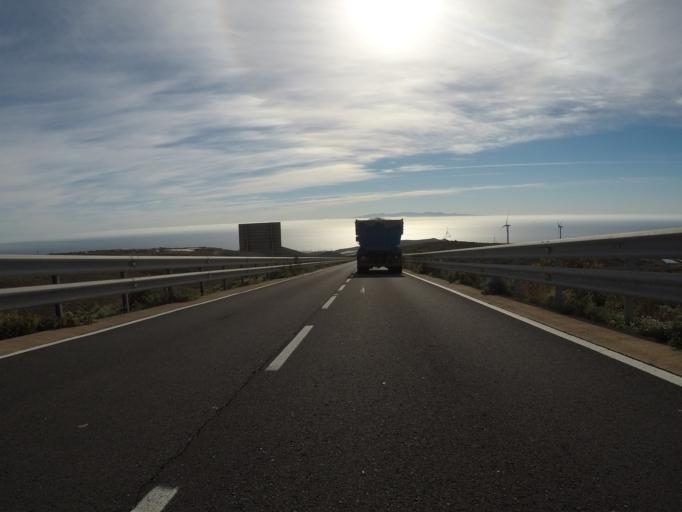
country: ES
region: Canary Islands
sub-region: Provincia de Santa Cruz de Tenerife
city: Lomo de Arico
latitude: 28.1613
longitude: -16.4884
